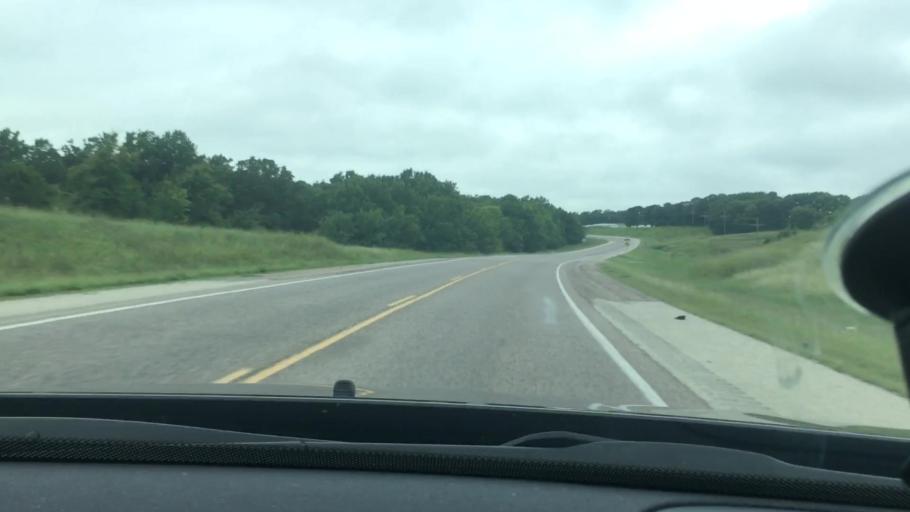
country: US
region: Oklahoma
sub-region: Pontotoc County
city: Ada
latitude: 34.7880
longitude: -96.5659
